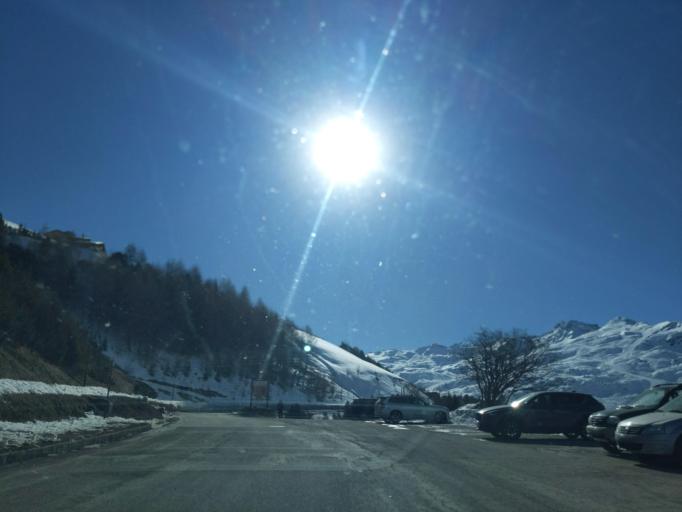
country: FR
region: Rhone-Alpes
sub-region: Departement de la Savoie
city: Val Thorens
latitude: 45.3195
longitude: 6.5400
